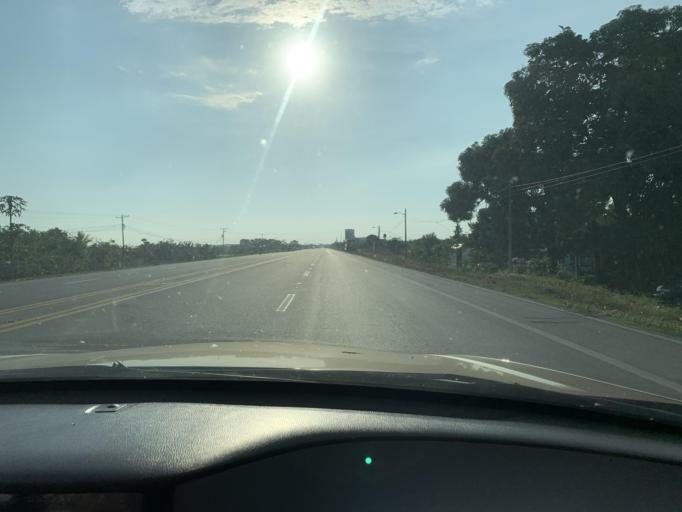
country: EC
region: Guayas
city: Naranjito
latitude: -2.2555
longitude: -79.6057
